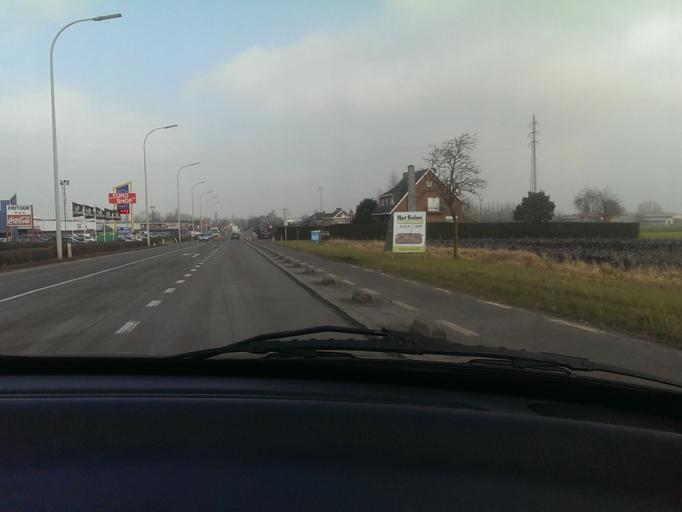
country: BE
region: Flanders
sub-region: Provincie West-Vlaanderen
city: Roeselare
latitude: 50.9032
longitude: 3.1151
